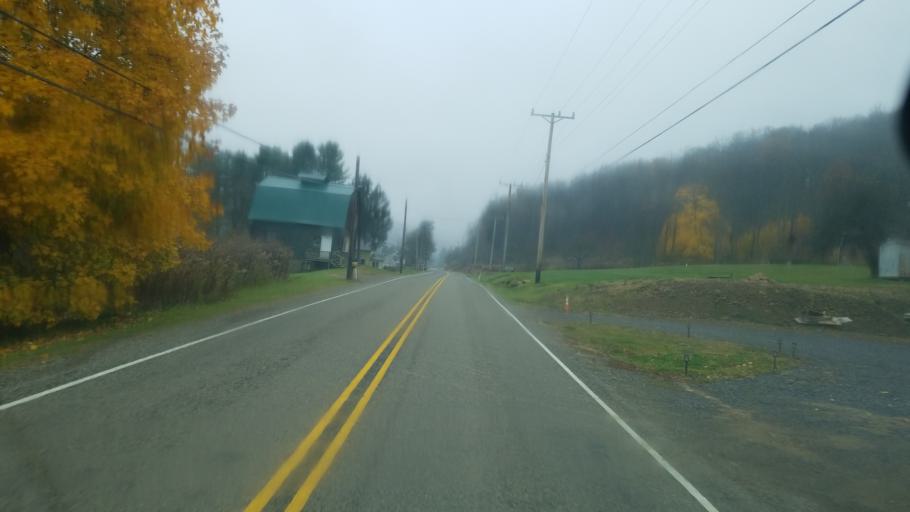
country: US
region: Pennsylvania
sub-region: McKean County
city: Smethport
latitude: 41.8910
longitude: -78.5057
